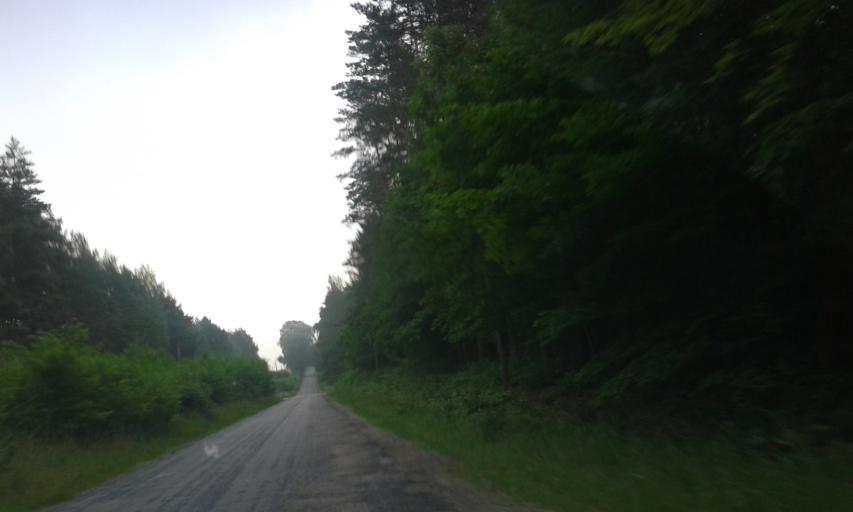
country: PL
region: Kujawsko-Pomorskie
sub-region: Powiat sepolenski
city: Sypniewo
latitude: 53.4494
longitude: 17.4033
